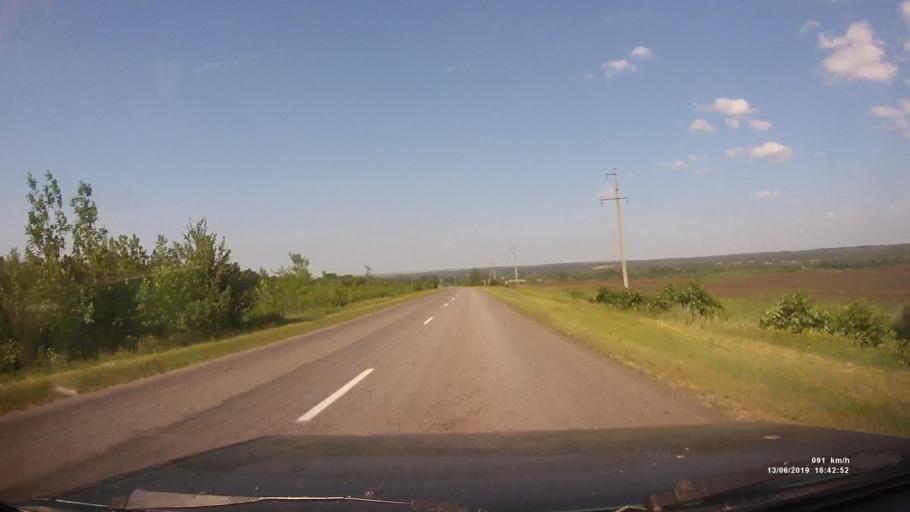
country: RU
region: Rostov
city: Kazanskaya
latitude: 49.9455
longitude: 41.4119
